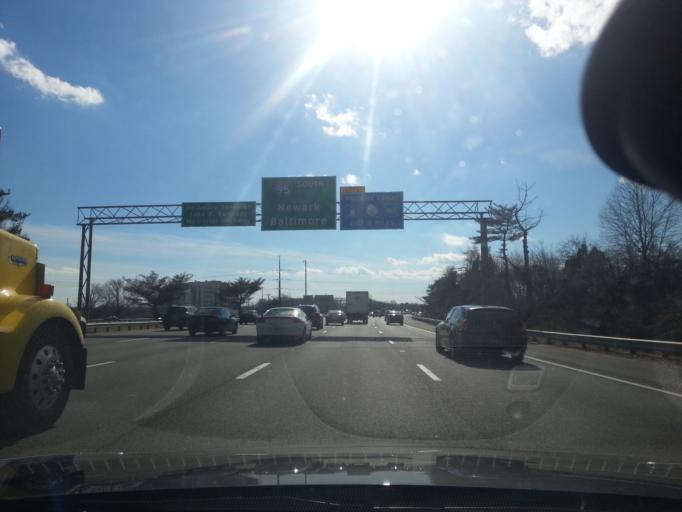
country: US
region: Delaware
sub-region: New Castle County
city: Newport
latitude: 39.6982
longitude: -75.6137
